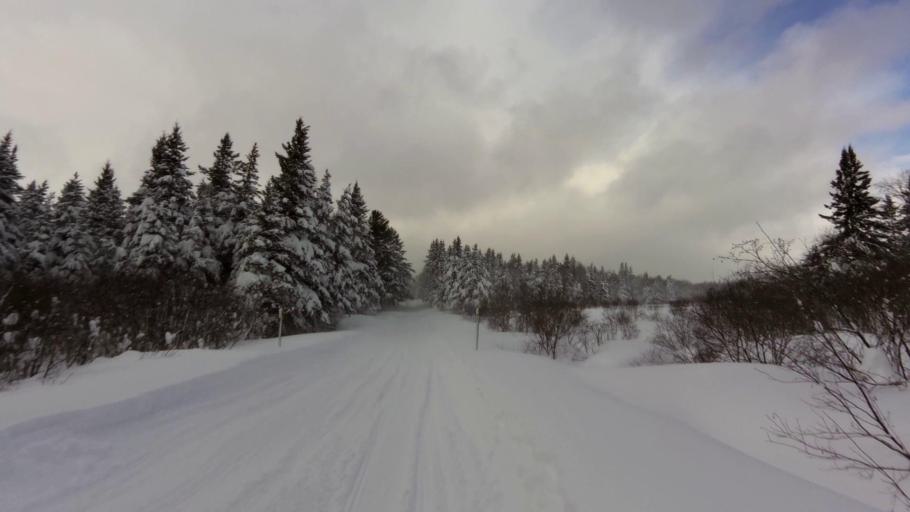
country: US
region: New York
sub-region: Lewis County
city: Lowville
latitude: 43.7415
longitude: -75.6730
